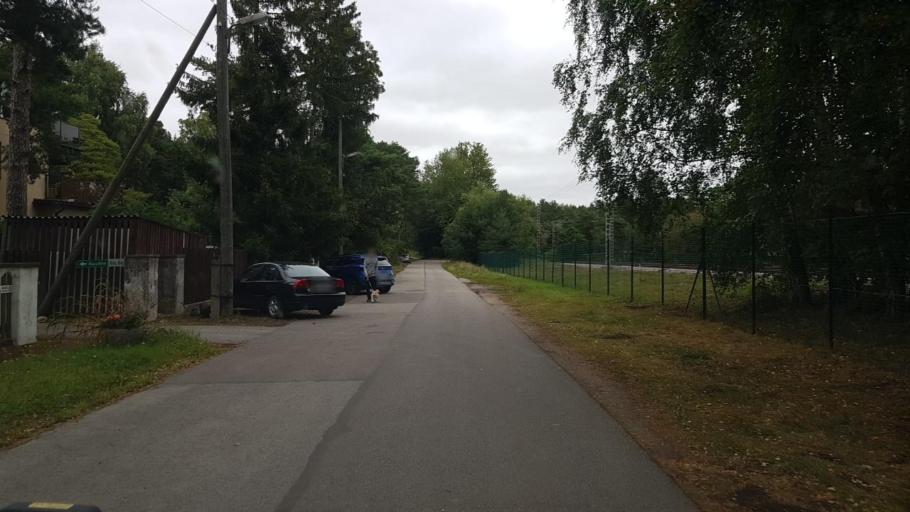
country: EE
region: Harju
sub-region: Tallinna linn
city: Tallinn
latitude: 59.3895
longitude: 24.7061
